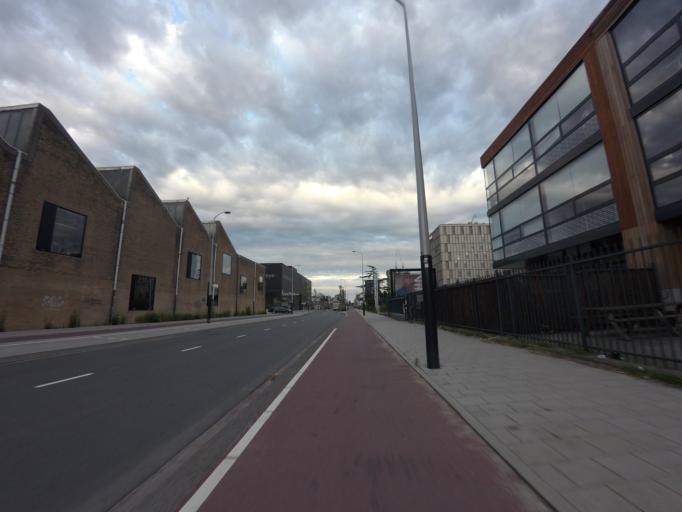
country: NL
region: North Holland
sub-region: Gemeente Amsterdam
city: Amsterdam
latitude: 52.3928
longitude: 4.9029
